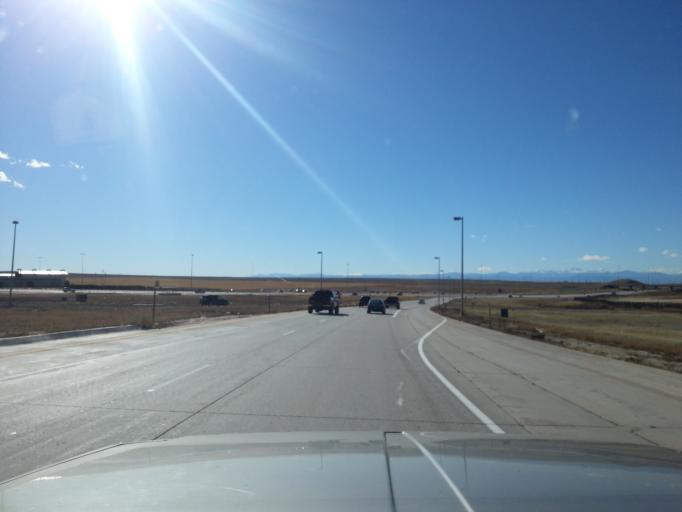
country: US
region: Colorado
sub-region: Adams County
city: Aurora
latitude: 39.8366
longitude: -104.7214
